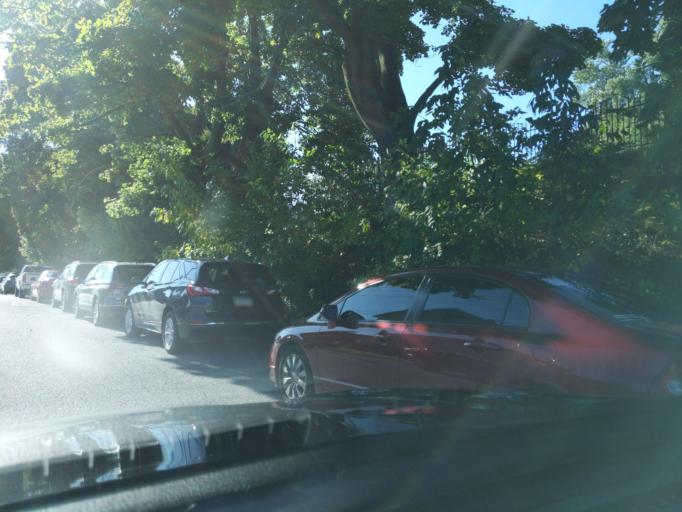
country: US
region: Pennsylvania
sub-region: Blair County
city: Altoona
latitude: 40.5238
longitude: -78.4003
